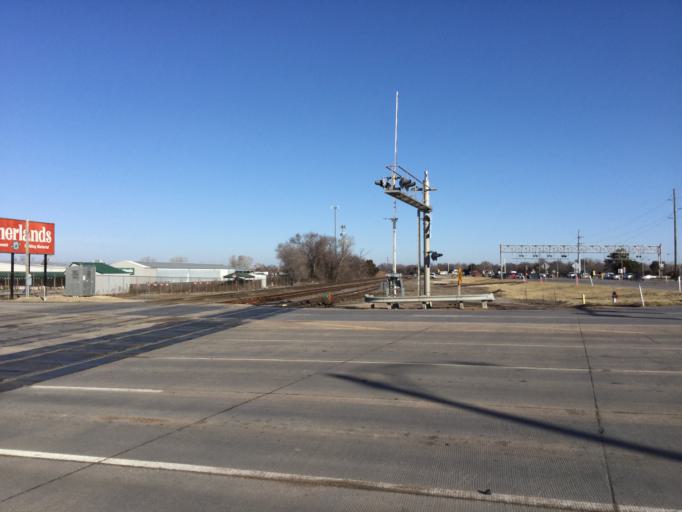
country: US
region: Kansas
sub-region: Sedgwick County
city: Derby
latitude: 37.6202
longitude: -97.2947
